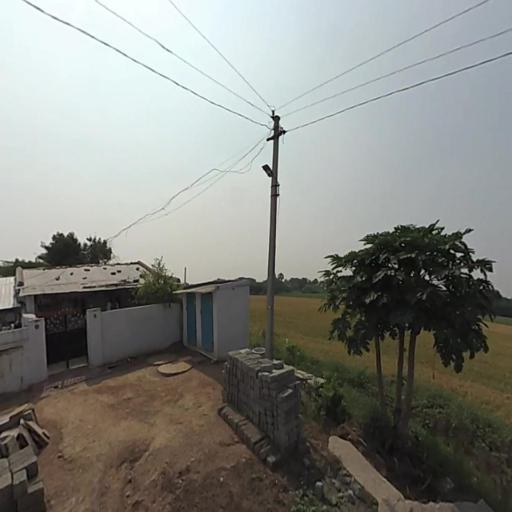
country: IN
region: Telangana
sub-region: Nalgonda
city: Nalgonda
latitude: 17.1846
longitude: 79.1258
